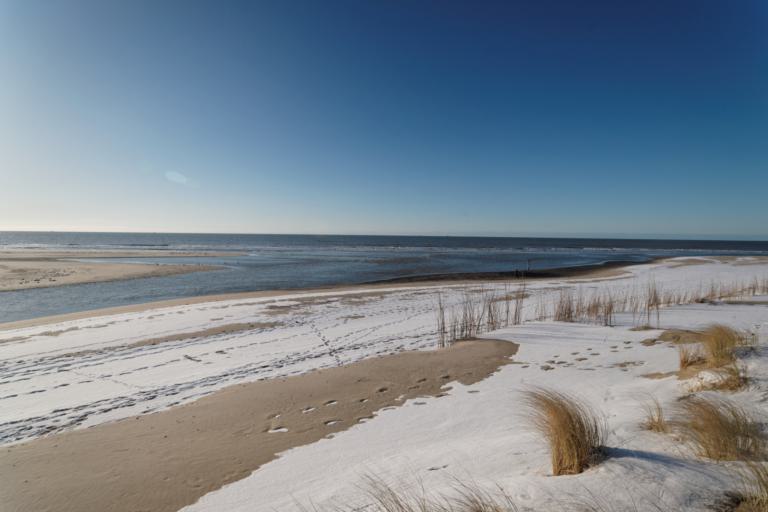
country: NL
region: North Holland
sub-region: Gemeente Texel
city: Den Burg
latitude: 53.1426
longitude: 4.8018
